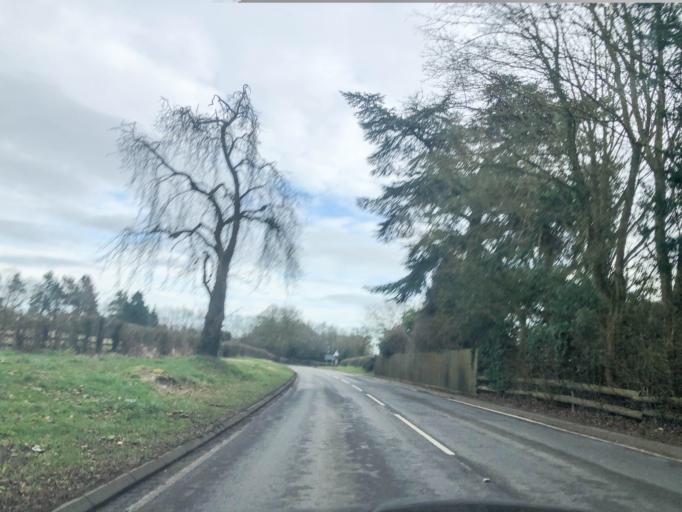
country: GB
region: England
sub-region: Warwickshire
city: Wroxall
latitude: 52.3043
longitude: -1.6820
